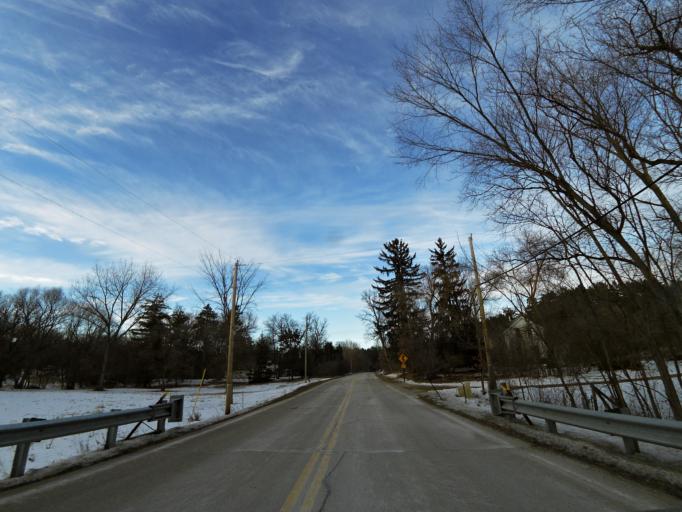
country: US
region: Minnesota
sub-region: Washington County
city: Afton
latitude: 44.9256
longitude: -92.8020
